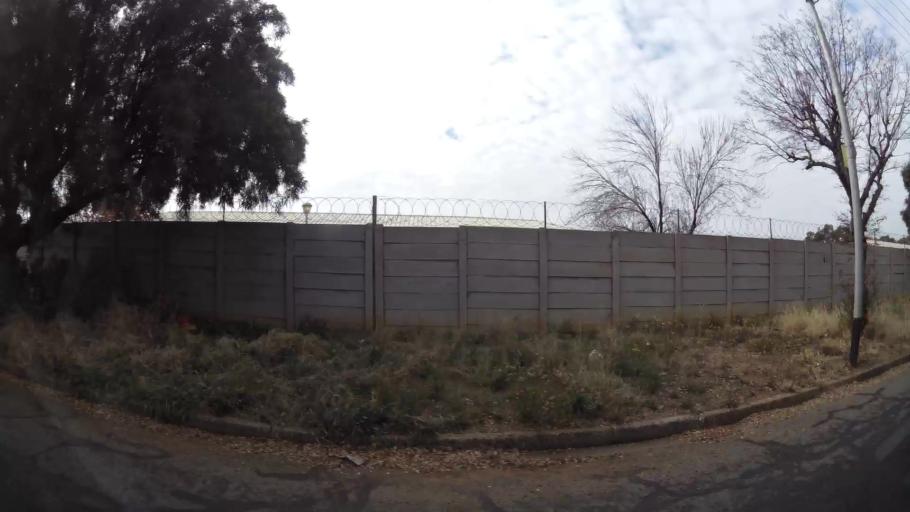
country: ZA
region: Orange Free State
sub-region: Mangaung Metropolitan Municipality
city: Bloemfontein
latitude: -29.1280
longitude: 26.1936
